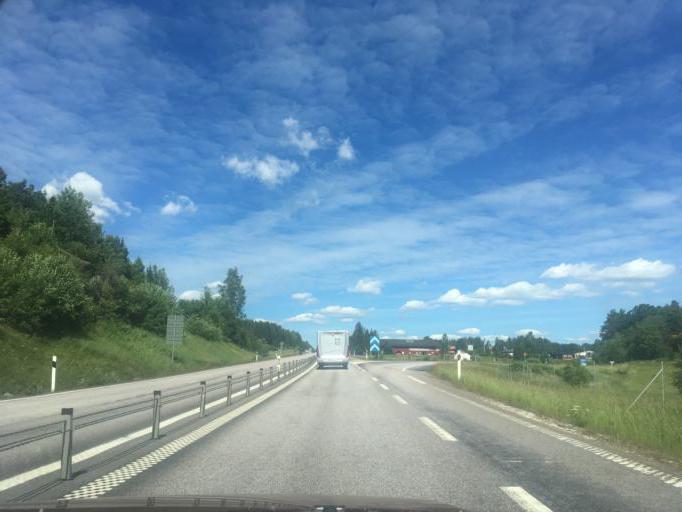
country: SE
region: OEstergoetland
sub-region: Valdemarsviks Kommun
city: Gusum
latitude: 58.2812
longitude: 16.5093
